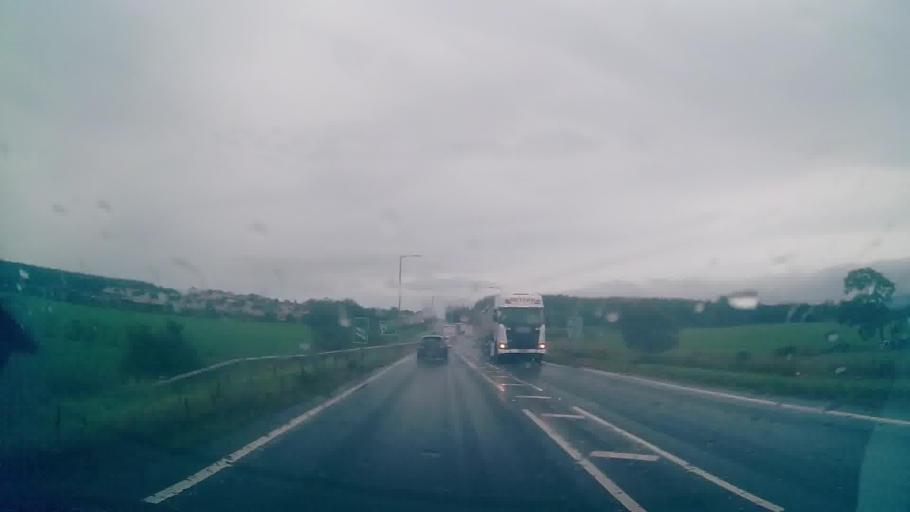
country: GB
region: Scotland
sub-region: East Ayrshire
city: Auchinleck
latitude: 55.4752
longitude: -4.3078
